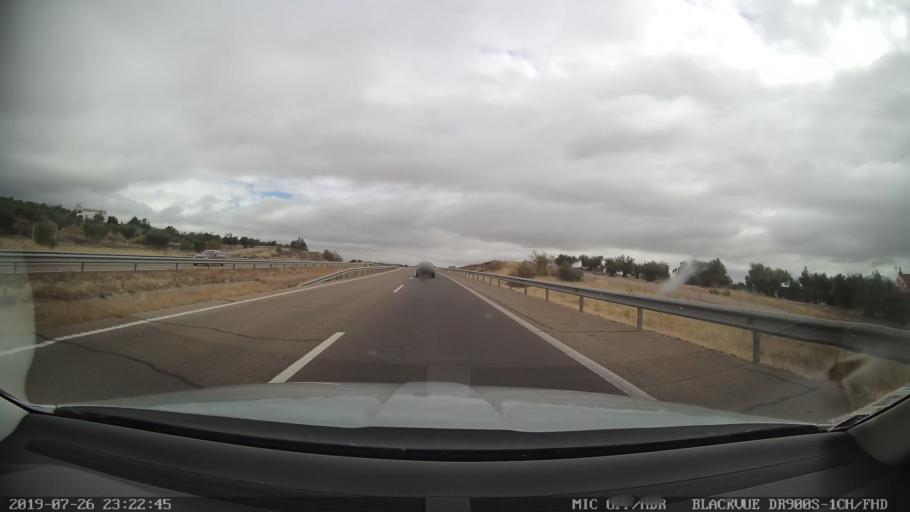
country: ES
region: Extremadura
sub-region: Provincia de Caceres
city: Miajadas
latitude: 39.1483
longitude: -5.9300
